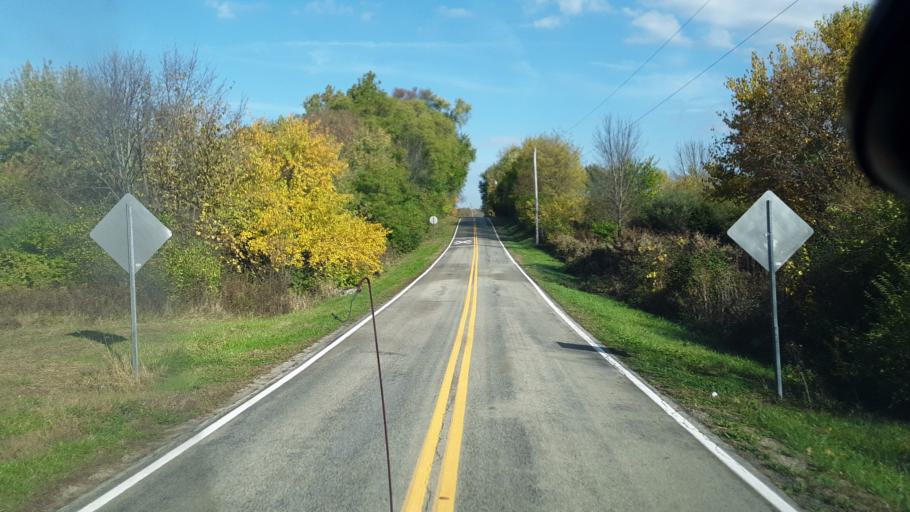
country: US
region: Ohio
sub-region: Highland County
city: Leesburg
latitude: 39.3392
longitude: -83.5849
